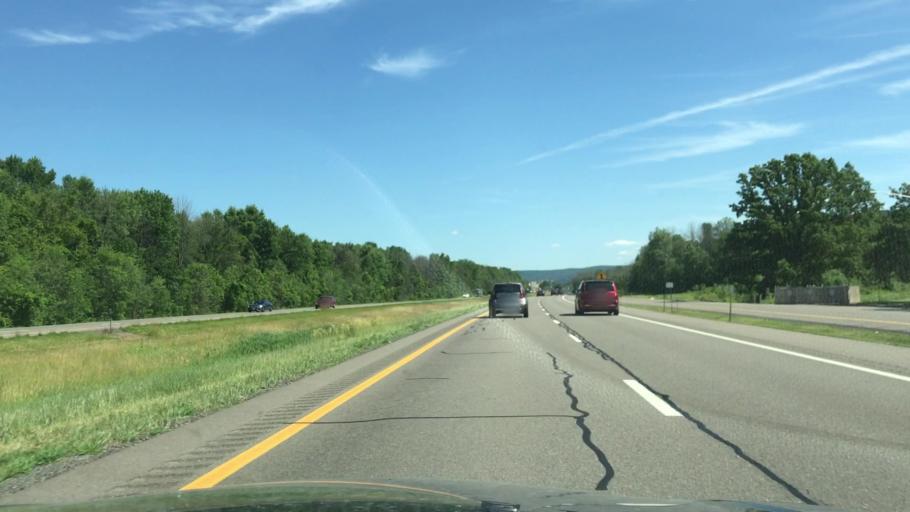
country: US
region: New York
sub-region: Steuben County
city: Gang Mills
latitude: 42.2433
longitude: -77.1979
